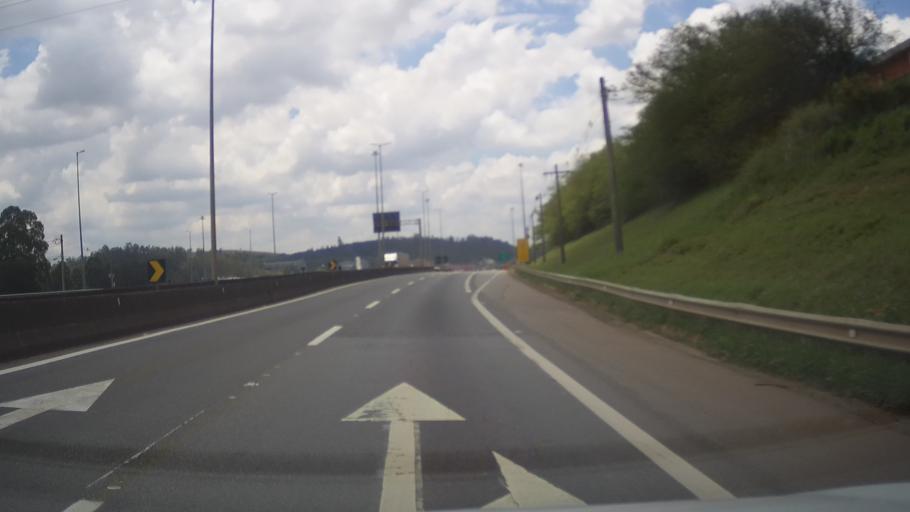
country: BR
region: Minas Gerais
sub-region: Tres Coracoes
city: Tres Coracoes
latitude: -21.6749
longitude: -45.3382
